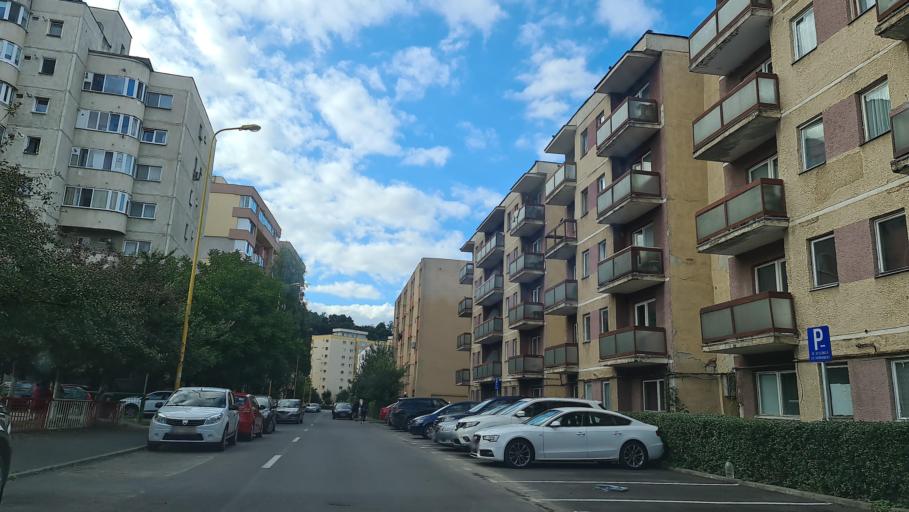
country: RO
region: Brasov
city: Brasov
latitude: 45.6432
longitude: 25.6208
